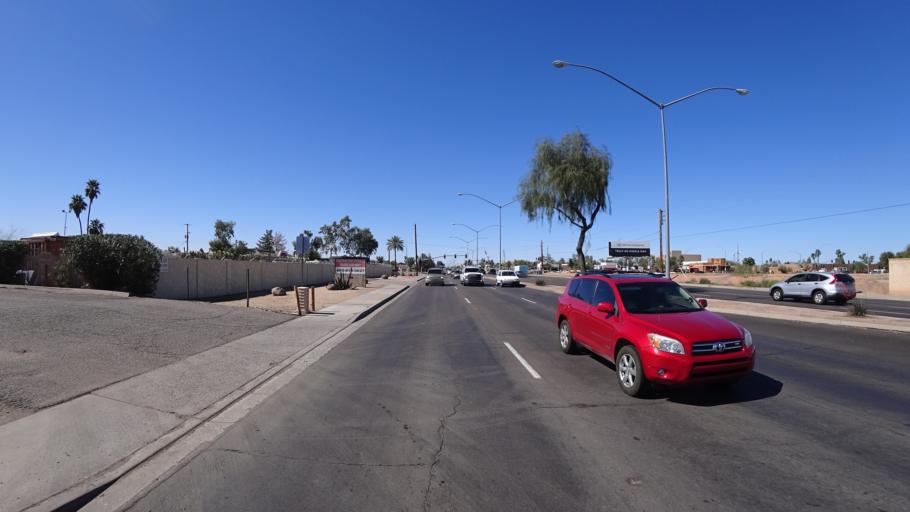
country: US
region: Arizona
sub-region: Maricopa County
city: San Carlos
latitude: 33.3788
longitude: -111.8234
